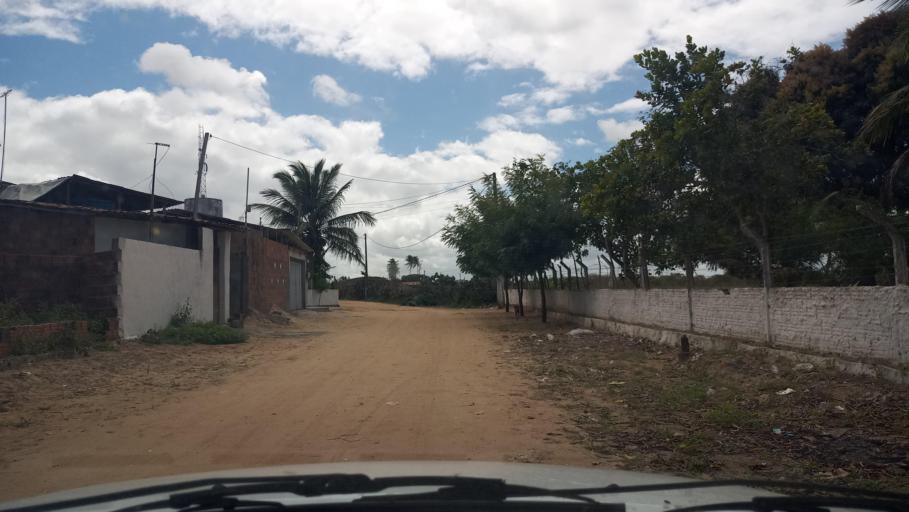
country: BR
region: Rio Grande do Norte
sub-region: Brejinho
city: Brejinho
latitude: -6.2069
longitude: -35.3459
